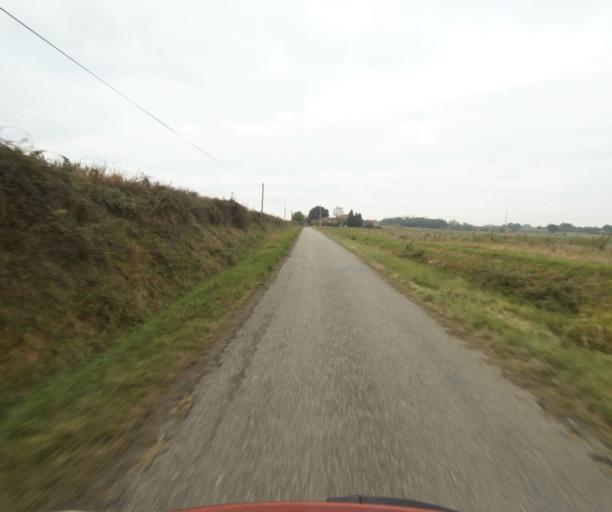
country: FR
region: Midi-Pyrenees
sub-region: Departement du Tarn-et-Garonne
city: Verdun-sur-Garonne
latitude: 43.8115
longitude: 1.2090
